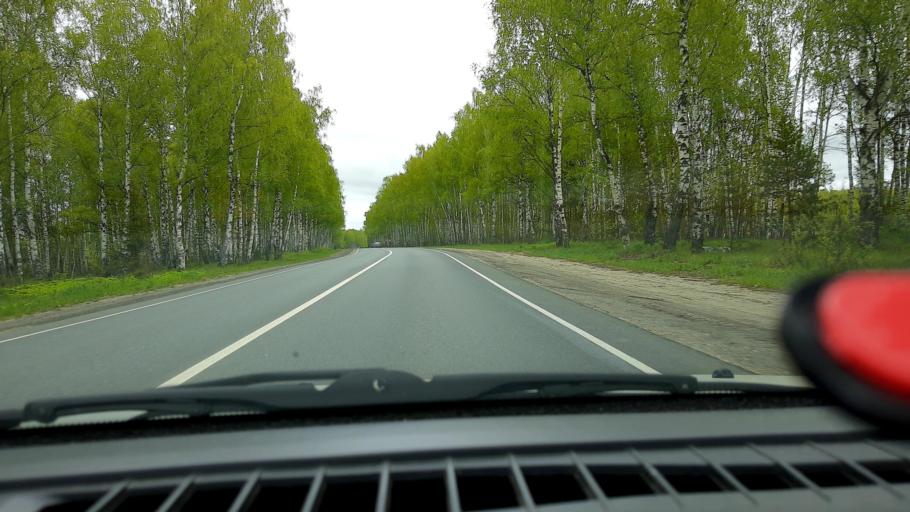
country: RU
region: Nizjnij Novgorod
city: Linda
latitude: 56.6709
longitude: 44.1413
